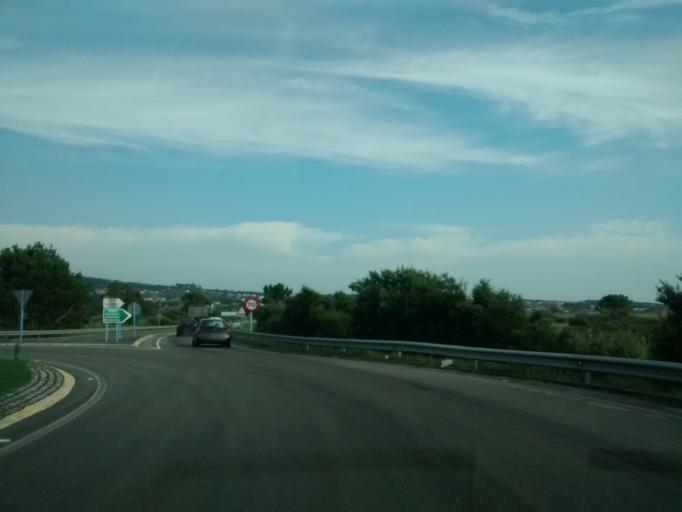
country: ES
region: Galicia
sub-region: Provincia de Pontevedra
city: O Grove
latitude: 42.4476
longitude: -8.8697
